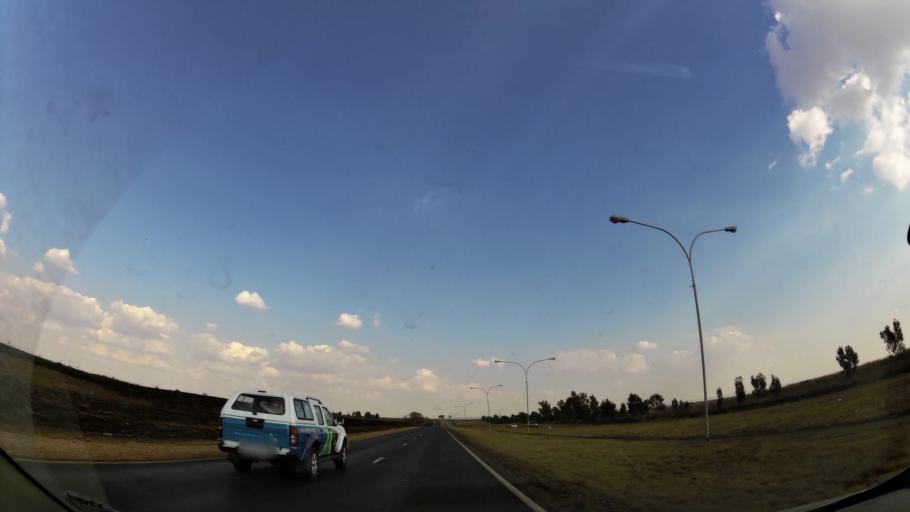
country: ZA
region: Gauteng
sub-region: Ekurhuleni Metropolitan Municipality
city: Springs
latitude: -26.3597
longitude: 28.3414
